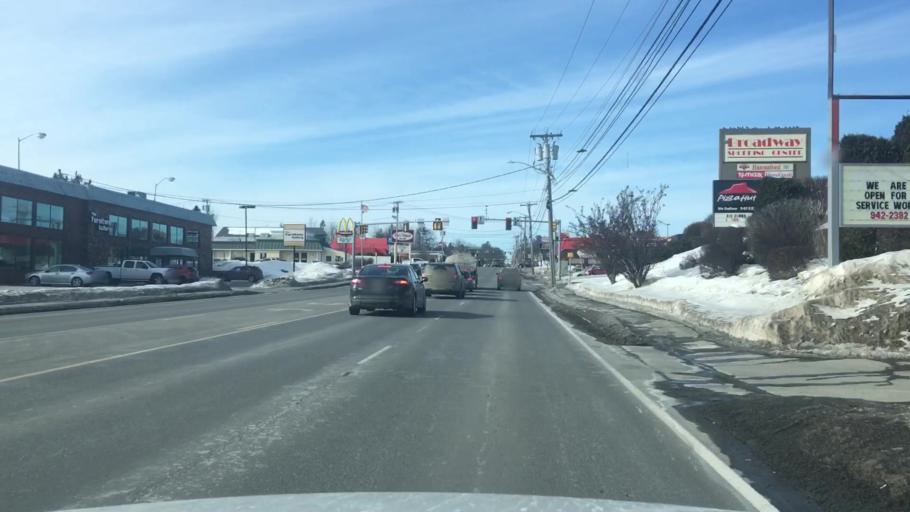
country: US
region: Maine
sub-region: Penobscot County
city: Bangor
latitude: 44.8217
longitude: -68.7776
